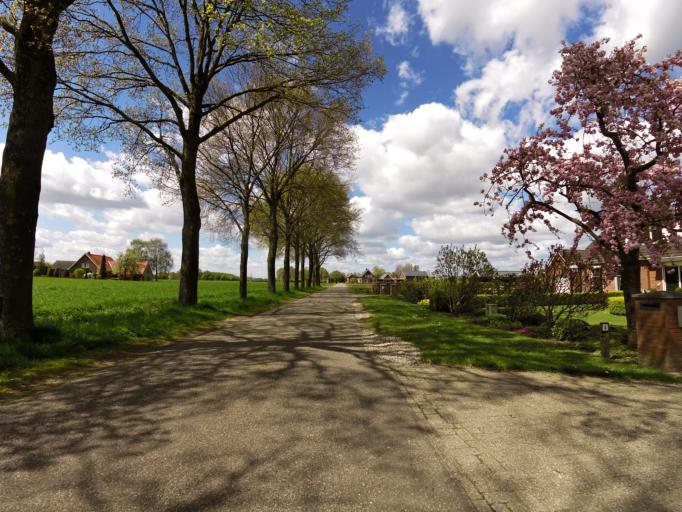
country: NL
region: Gelderland
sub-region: Gemeente Doetinchem
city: Doetinchem
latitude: 51.9407
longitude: 6.2213
